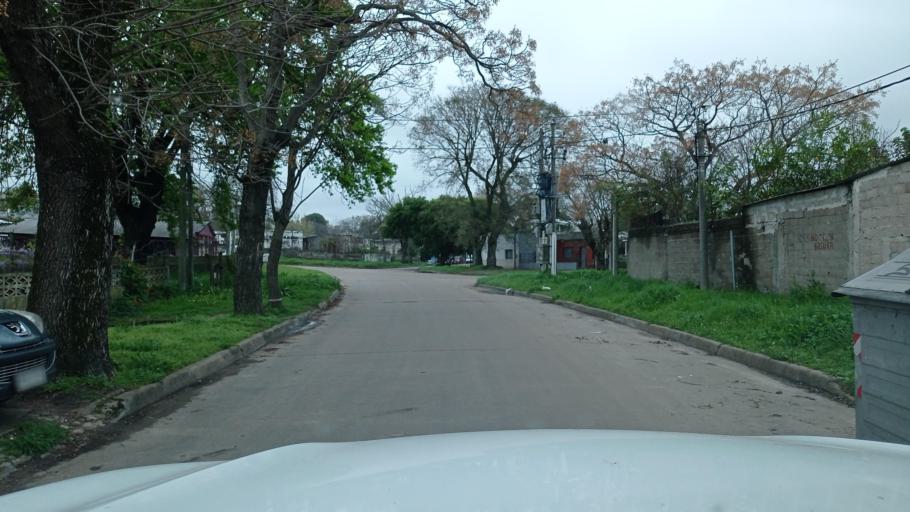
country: UY
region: Montevideo
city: Montevideo
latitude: -34.8483
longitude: -56.2157
